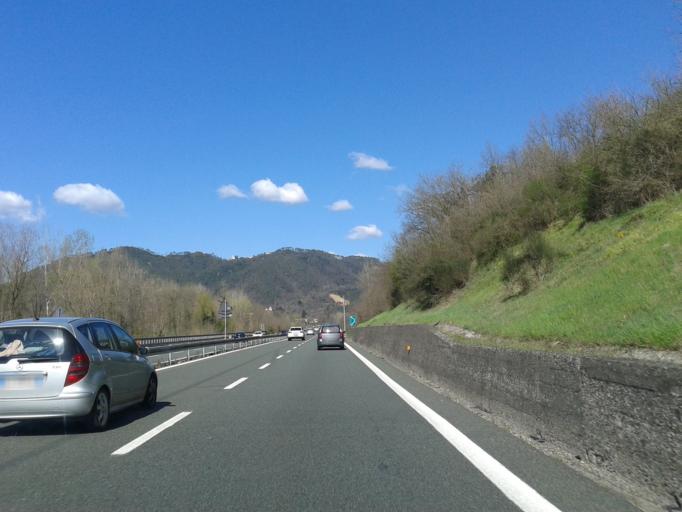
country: IT
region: Liguria
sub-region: Provincia di La Spezia
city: Beverino
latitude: 44.2010
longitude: 9.8069
